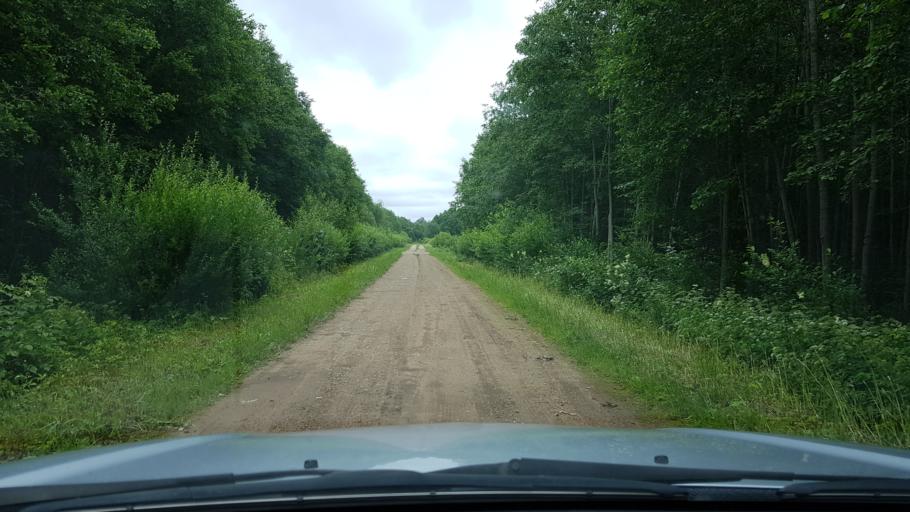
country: EE
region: Ida-Virumaa
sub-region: Narva-Joesuu linn
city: Narva-Joesuu
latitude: 59.3429
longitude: 27.9583
